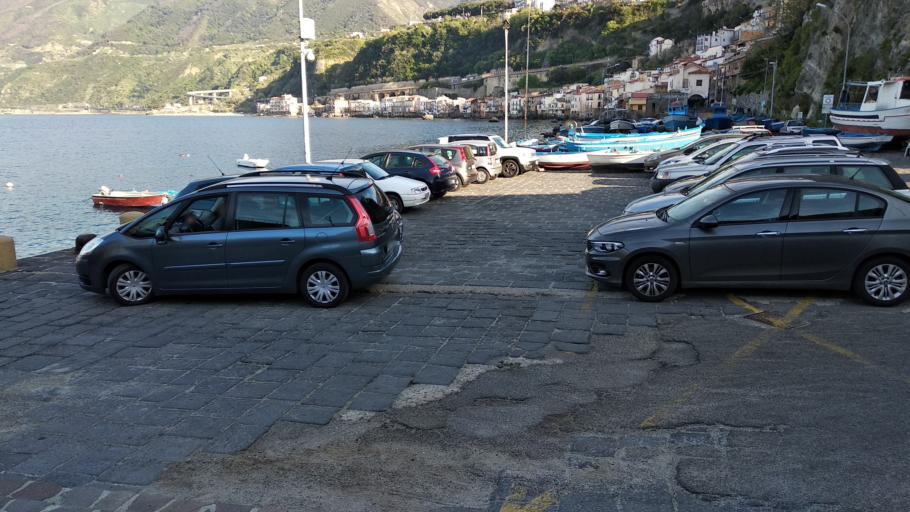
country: IT
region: Calabria
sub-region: Provincia di Reggio Calabria
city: Scilla
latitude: 38.2569
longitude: 15.7146
